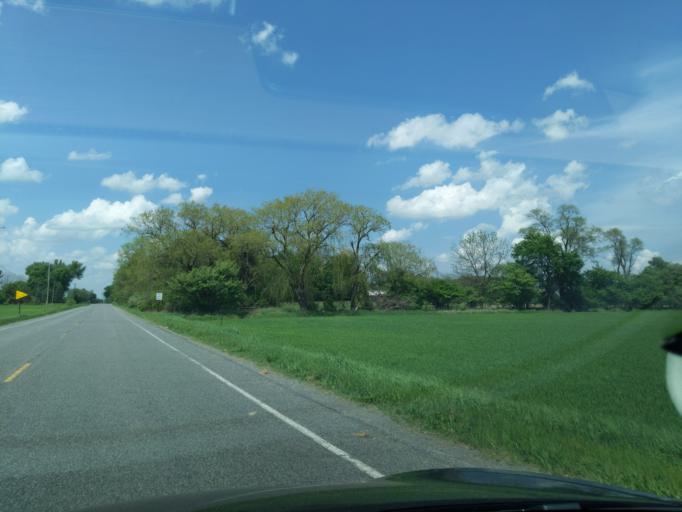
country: US
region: Michigan
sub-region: Ingham County
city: Mason
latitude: 42.5994
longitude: -84.4329
